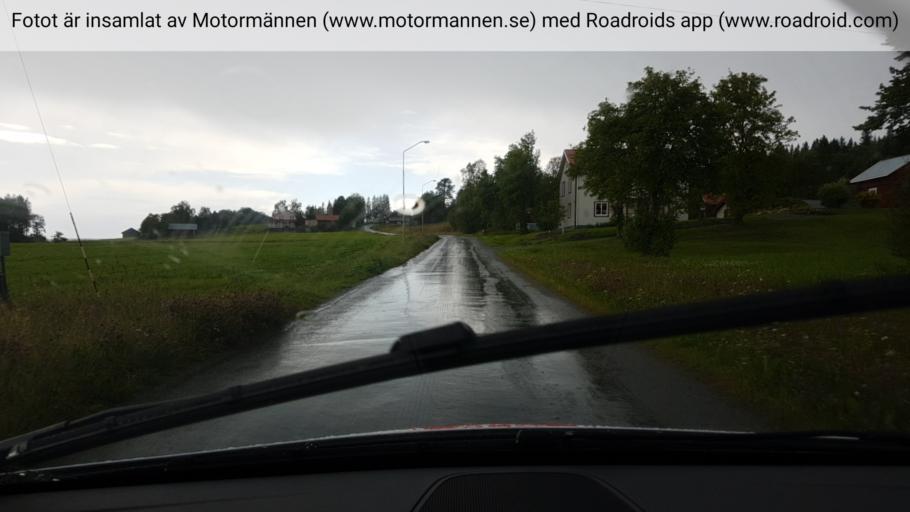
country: SE
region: Jaemtland
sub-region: OEstersunds Kommun
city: Brunflo
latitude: 63.0308
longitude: 14.7812
